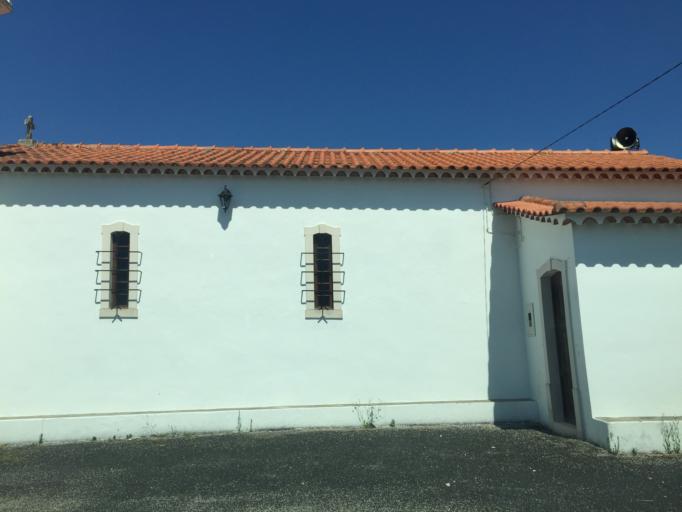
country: PT
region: Santarem
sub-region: Ferreira do Zezere
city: Ferreira do Zezere
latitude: 39.6407
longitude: -8.3364
